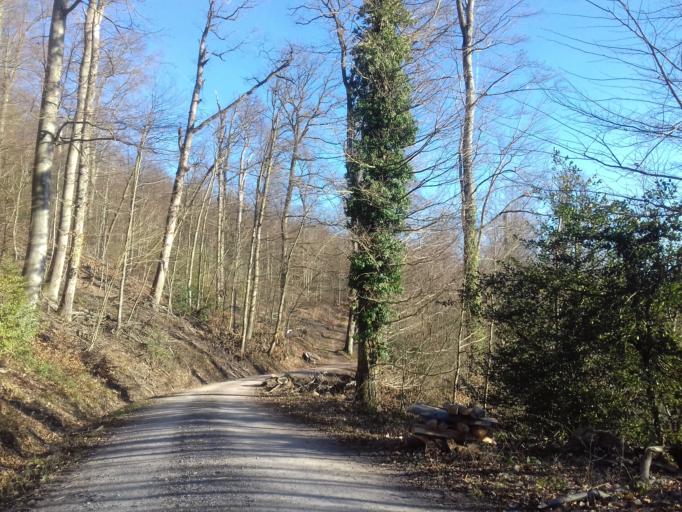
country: DE
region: Baden-Wuerttemberg
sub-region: Karlsruhe Region
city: Baden-Baden
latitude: 48.7750
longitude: 8.2410
